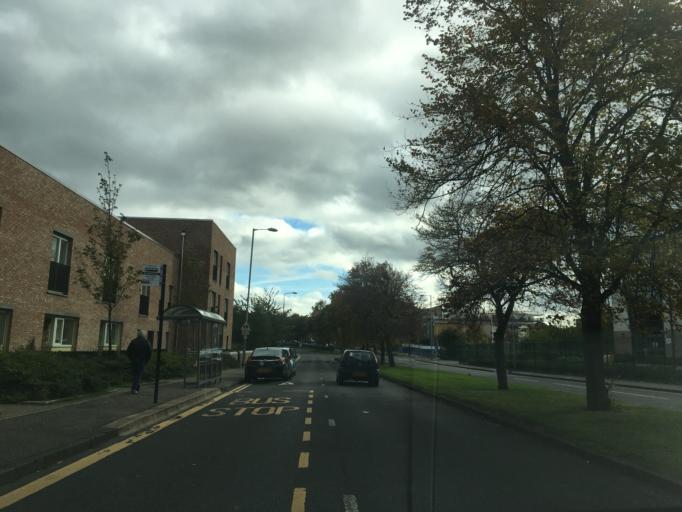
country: GB
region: Scotland
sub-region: Edinburgh
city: Edinburgh
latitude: 55.9736
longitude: -3.2531
